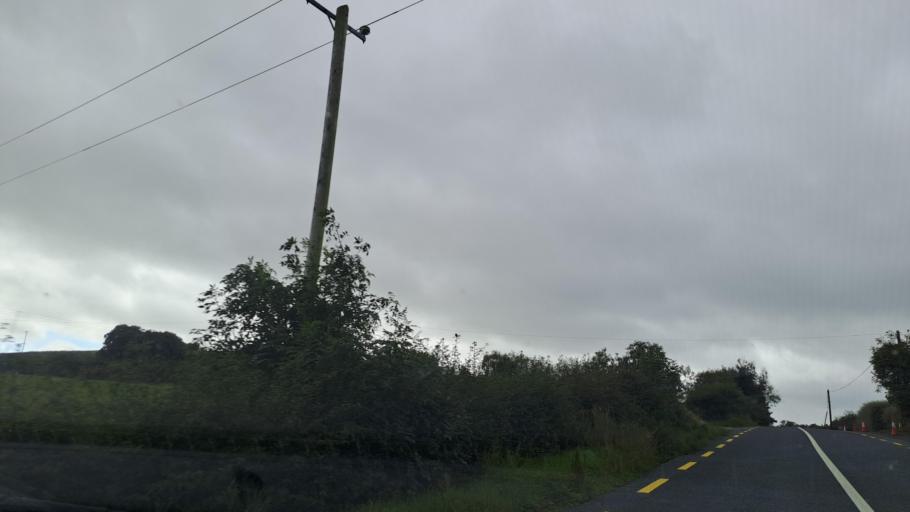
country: IE
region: Ulster
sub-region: An Cabhan
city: Bailieborough
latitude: 53.9553
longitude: -6.9463
